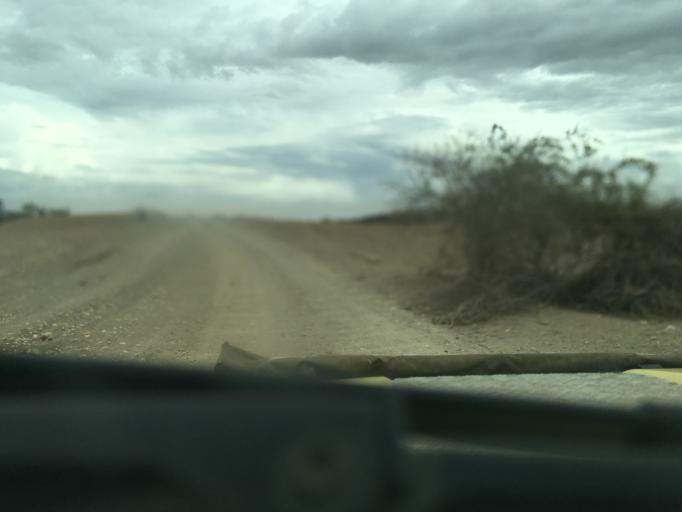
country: KE
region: Kajiado
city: Magadi
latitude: -2.5025
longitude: 35.8738
